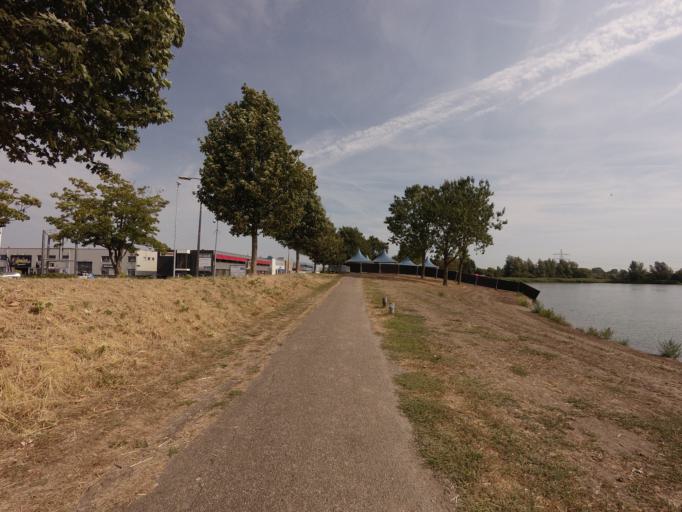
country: NL
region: Utrecht
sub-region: Gemeente Nieuwegein
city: Nieuwegein
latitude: 52.0767
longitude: 5.0574
